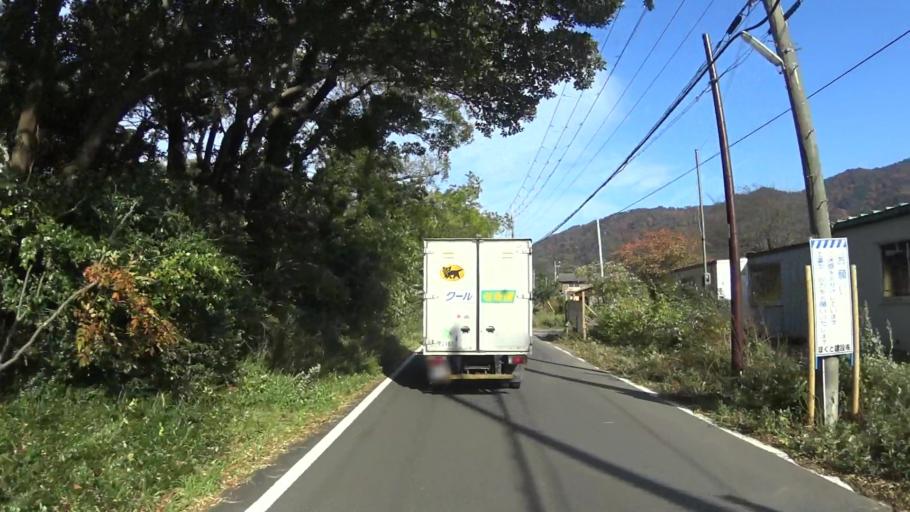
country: JP
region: Kyoto
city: Maizuru
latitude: 35.5586
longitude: 135.3977
